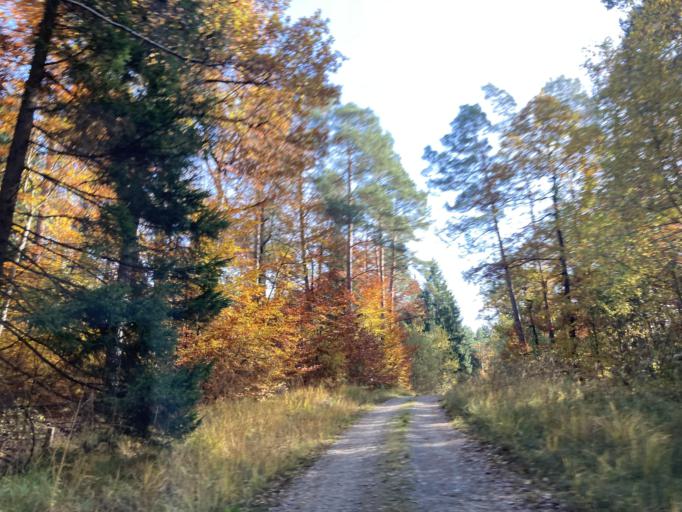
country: DE
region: Baden-Wuerttemberg
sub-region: Tuebingen Region
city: Bodelshausen
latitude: 48.4152
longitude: 8.9561
